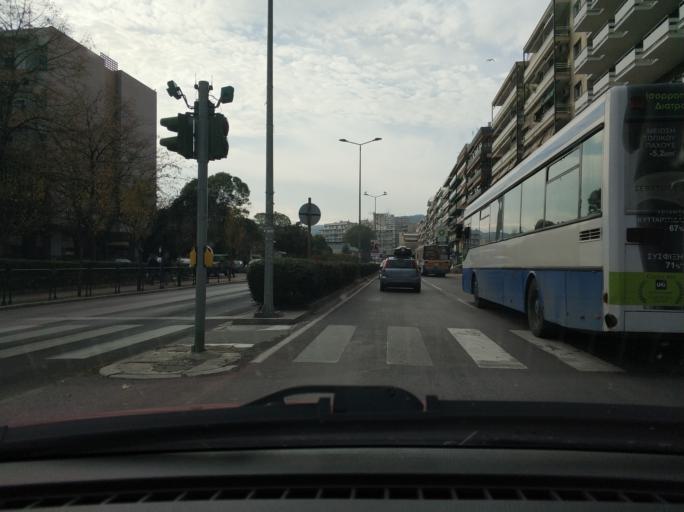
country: GR
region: East Macedonia and Thrace
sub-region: Nomos Kavalas
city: Kavala
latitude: 40.9364
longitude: 24.4061
